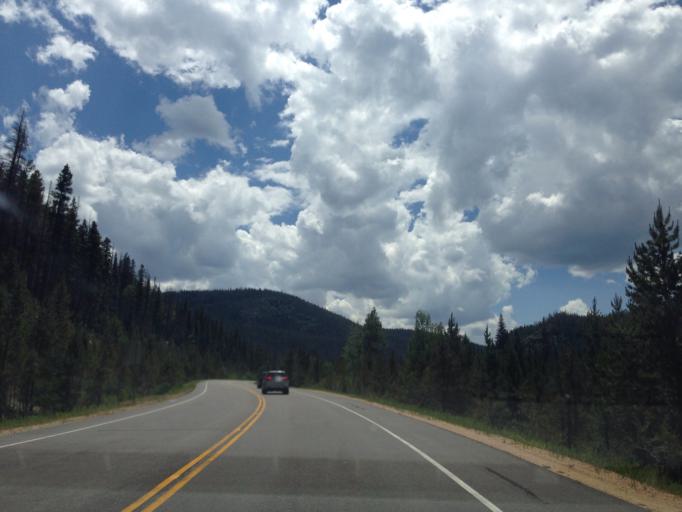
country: US
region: Colorado
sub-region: Larimer County
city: Estes Park
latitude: 40.6247
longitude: -105.8161
